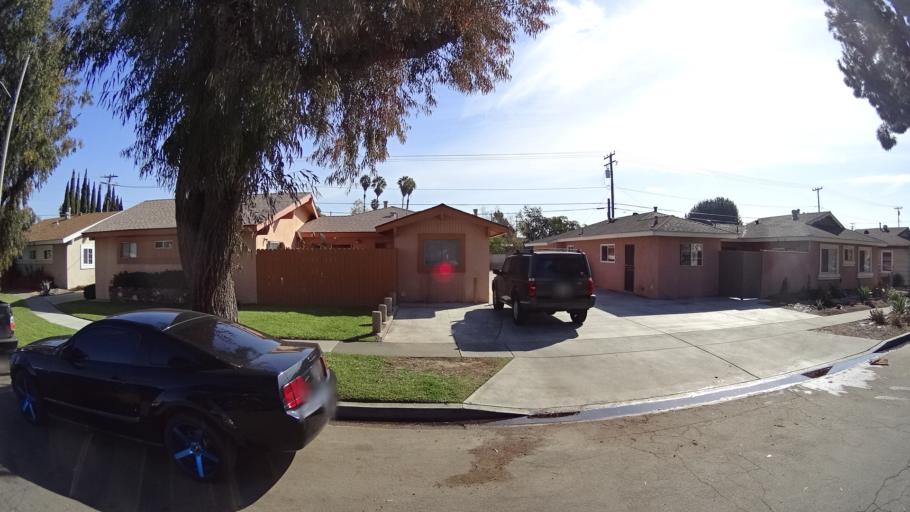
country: US
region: California
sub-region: Orange County
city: Fullerton
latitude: 33.8521
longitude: -117.9401
